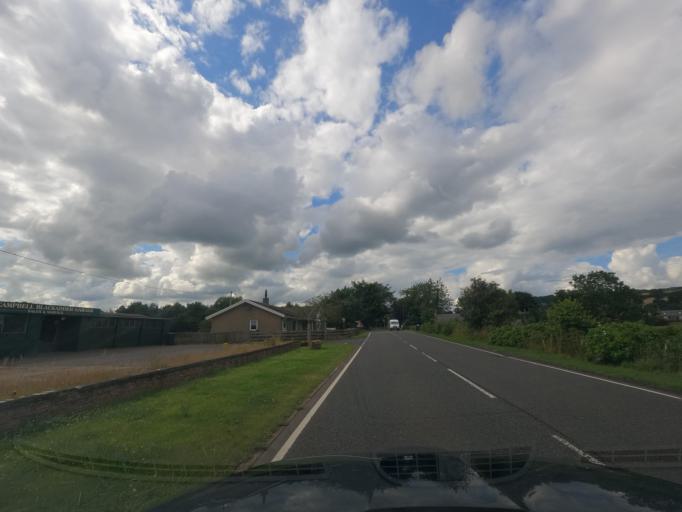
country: GB
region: Scotland
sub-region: The Scottish Borders
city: Kelso
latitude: 55.7056
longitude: -2.4537
